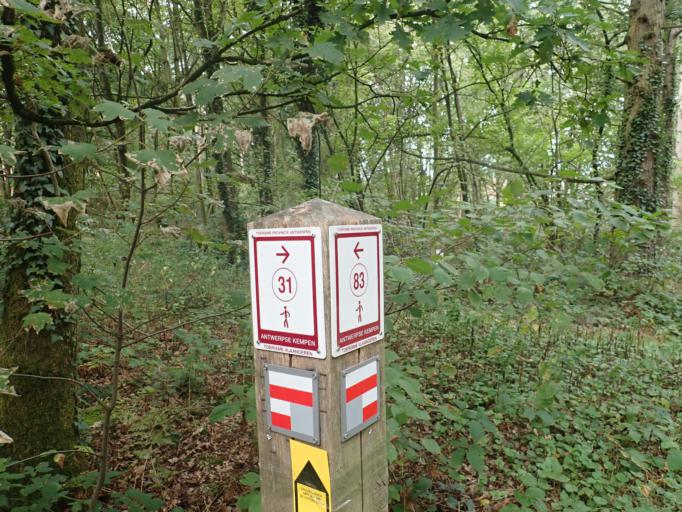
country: BE
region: Flanders
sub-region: Provincie Antwerpen
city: Brasschaat
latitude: 51.3144
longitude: 4.5219
